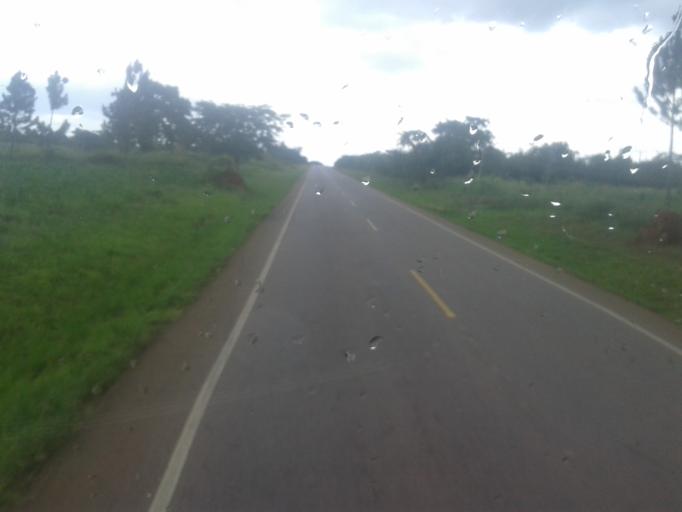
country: UG
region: Central Region
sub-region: Nakasongola District
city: Nakasongola
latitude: 1.3369
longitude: 32.4076
